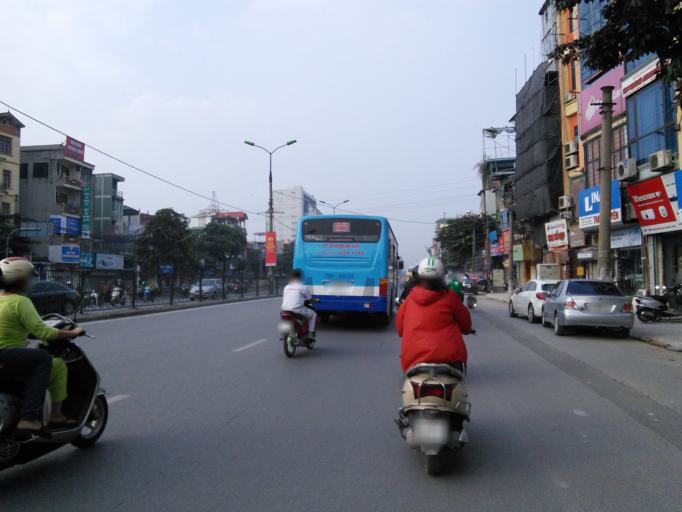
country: VN
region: Ha Noi
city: Hai BaTrung
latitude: 20.9905
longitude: 105.8412
